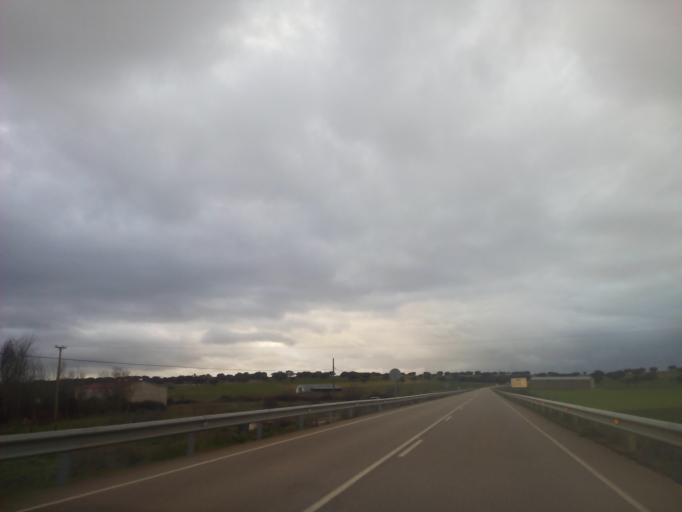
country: ES
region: Castille and Leon
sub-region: Provincia de Salamanca
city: Cabrillas
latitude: 40.7430
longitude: -6.1781
